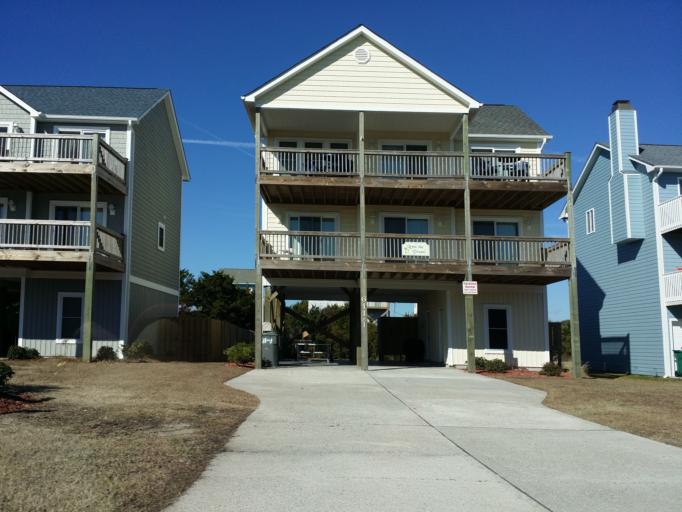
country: US
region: North Carolina
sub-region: Pender County
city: Surf City
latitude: 34.4217
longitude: -77.5517
